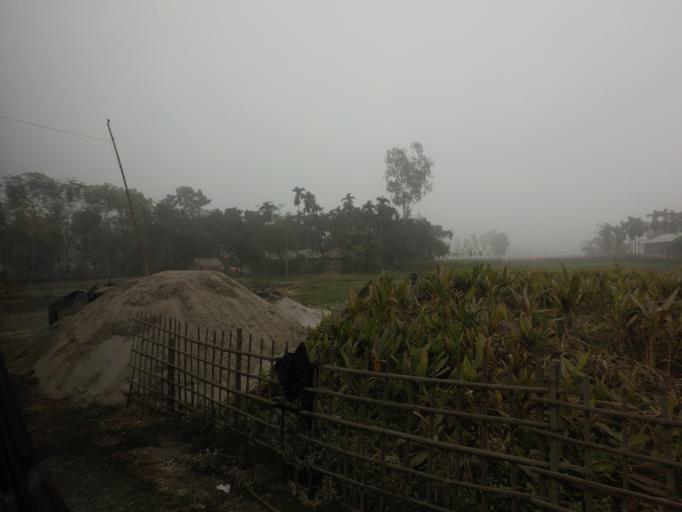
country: BD
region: Rajshahi
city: Saidpur
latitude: 25.9218
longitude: 88.8658
